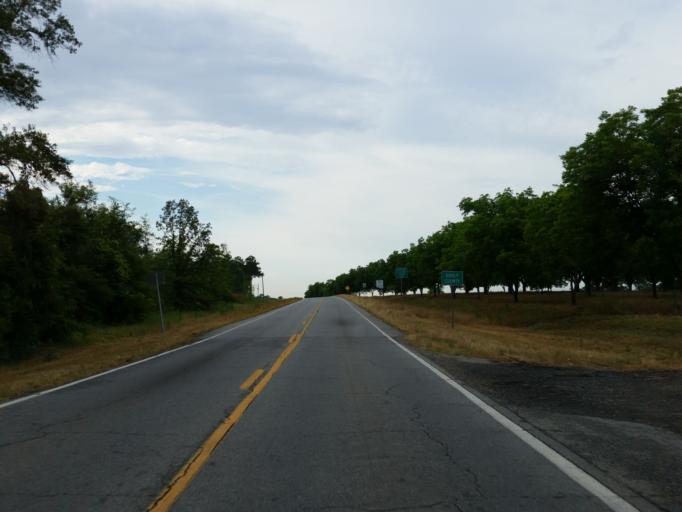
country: US
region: Georgia
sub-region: Dooly County
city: Vienna
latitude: 32.0292
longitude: -83.7920
